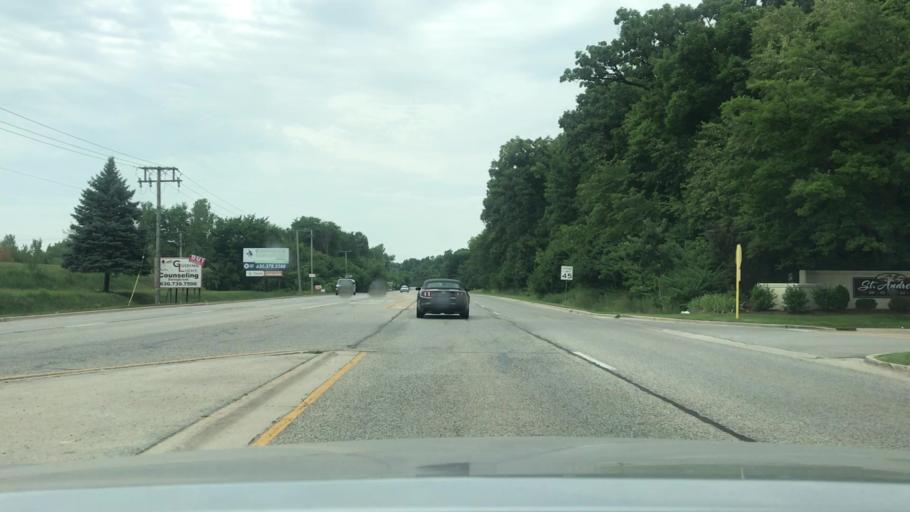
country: US
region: Illinois
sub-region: DuPage County
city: Woodridge
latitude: 41.7253
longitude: -88.0643
